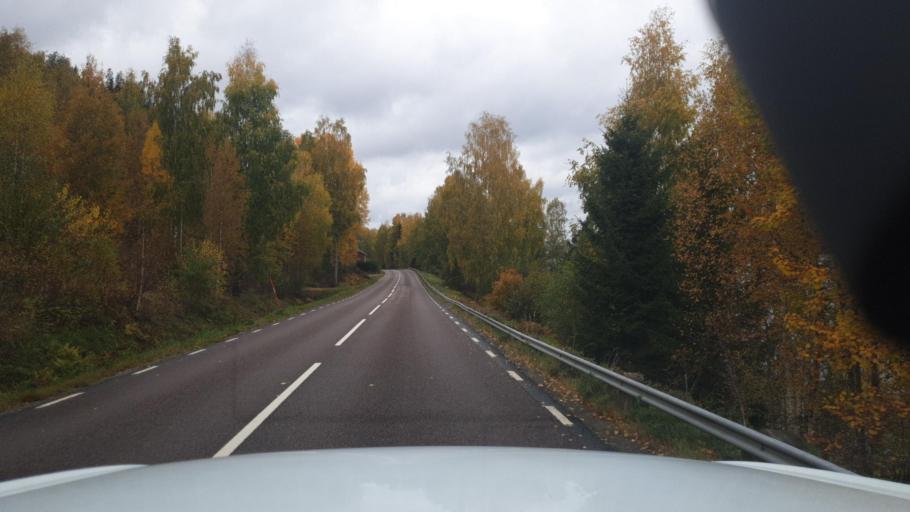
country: SE
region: Vaermland
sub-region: Sunne Kommun
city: Sunne
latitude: 59.8161
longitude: 13.0140
